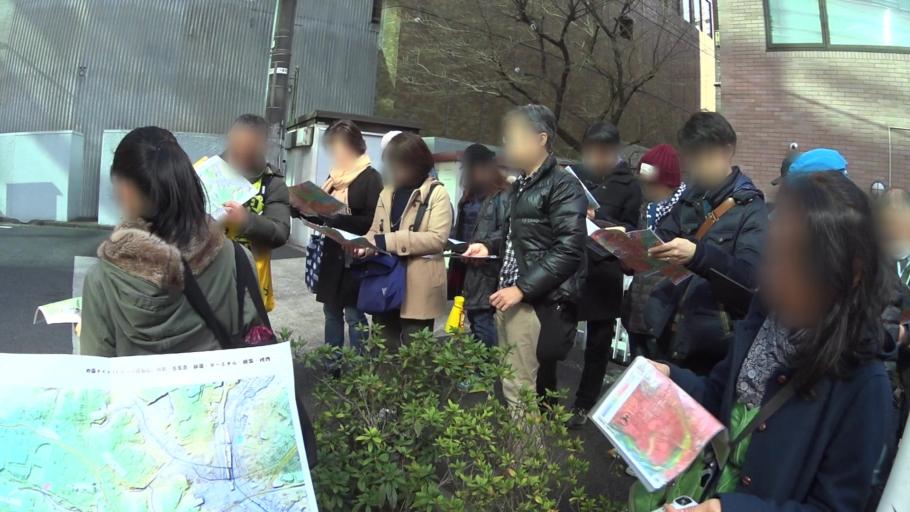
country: JP
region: Tokyo
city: Tokyo
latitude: 35.6536
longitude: 139.6896
